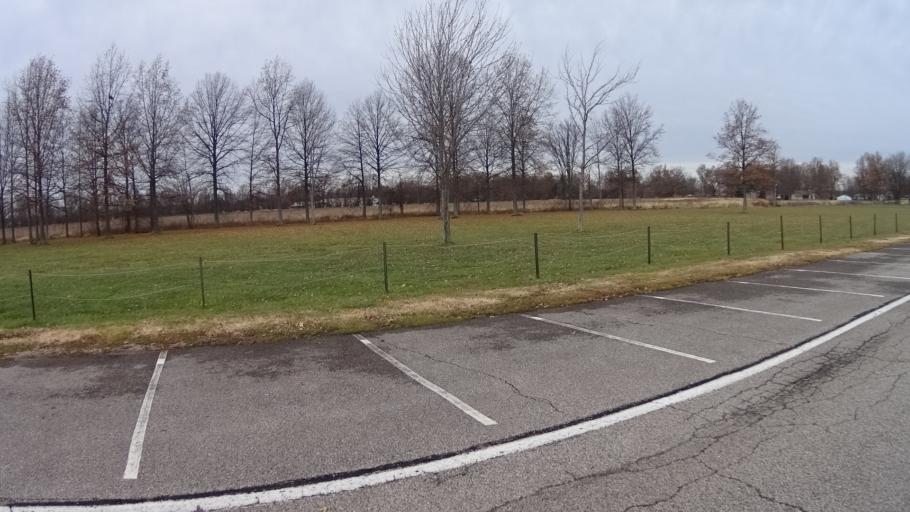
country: US
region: Ohio
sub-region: Lorain County
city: North Ridgeville
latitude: 41.3688
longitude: -82.0334
